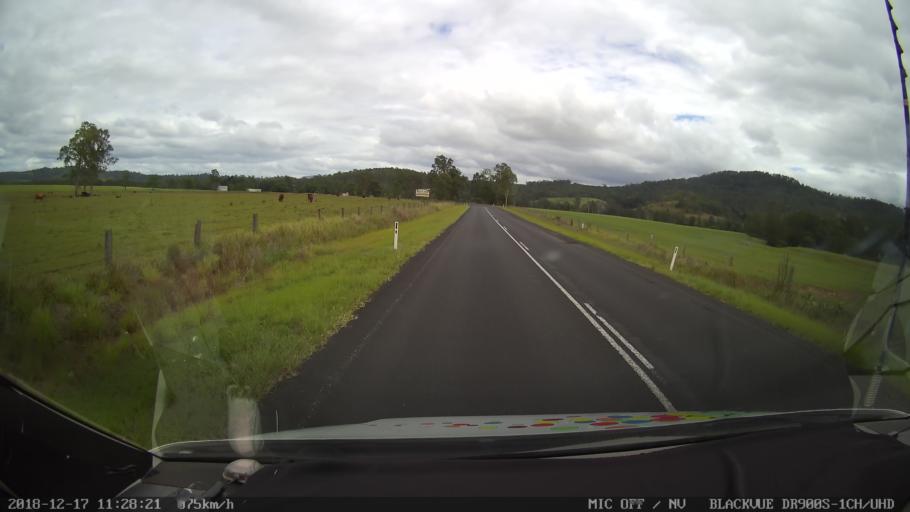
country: AU
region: New South Wales
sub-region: Kyogle
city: Kyogle
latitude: -28.7435
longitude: 152.6377
